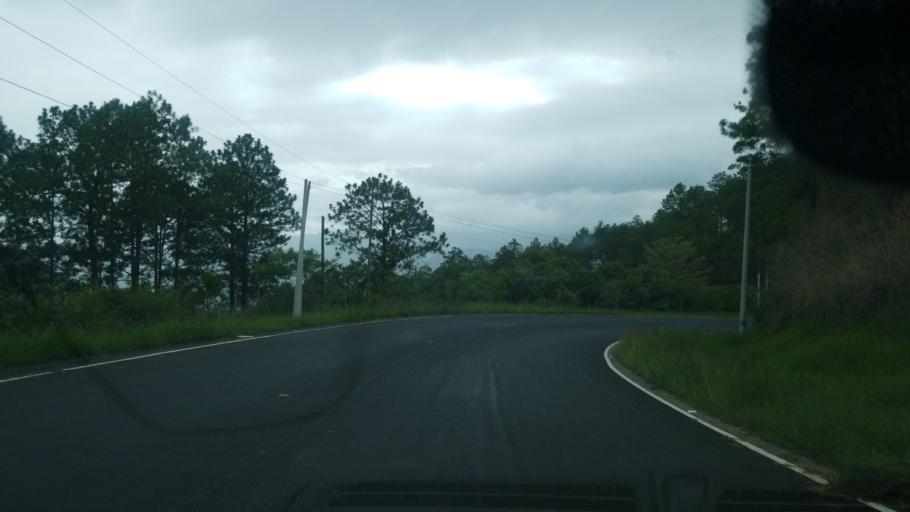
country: HN
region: Ocotepeque
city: Sinuapa
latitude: 14.4560
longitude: -89.1500
